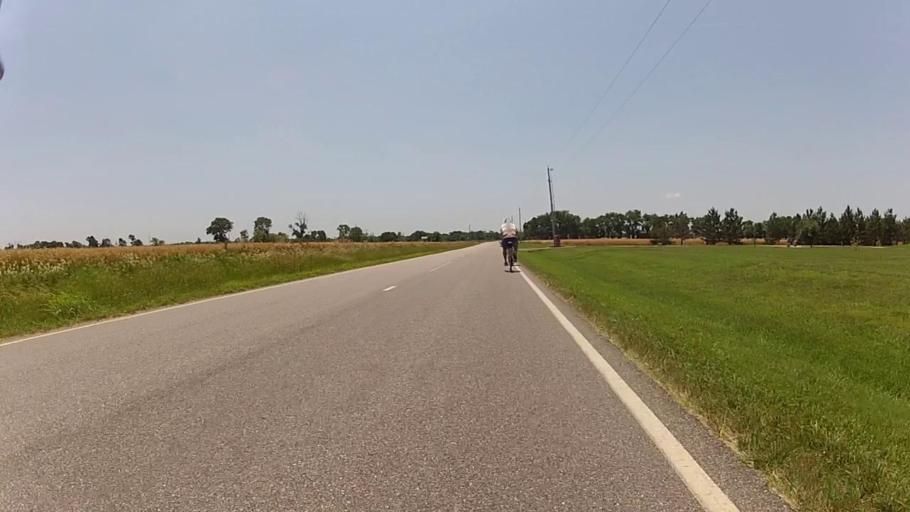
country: US
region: Kansas
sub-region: Montgomery County
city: Cherryvale
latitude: 37.2547
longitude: -95.5370
